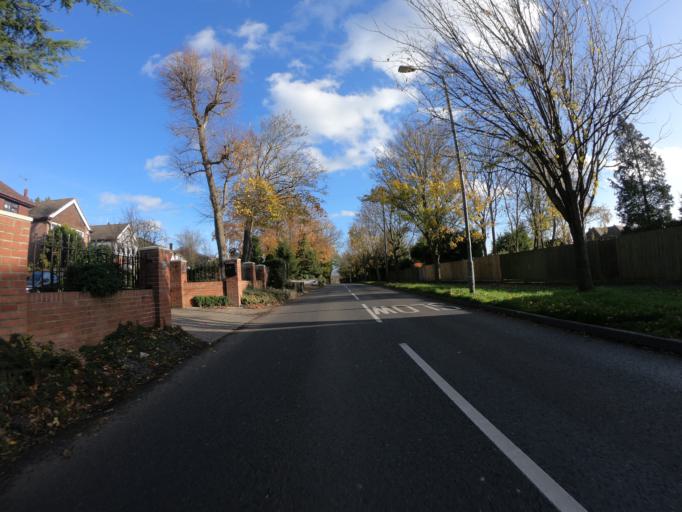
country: GB
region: England
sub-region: Greater London
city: Orpington
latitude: 51.3988
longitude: 0.0972
